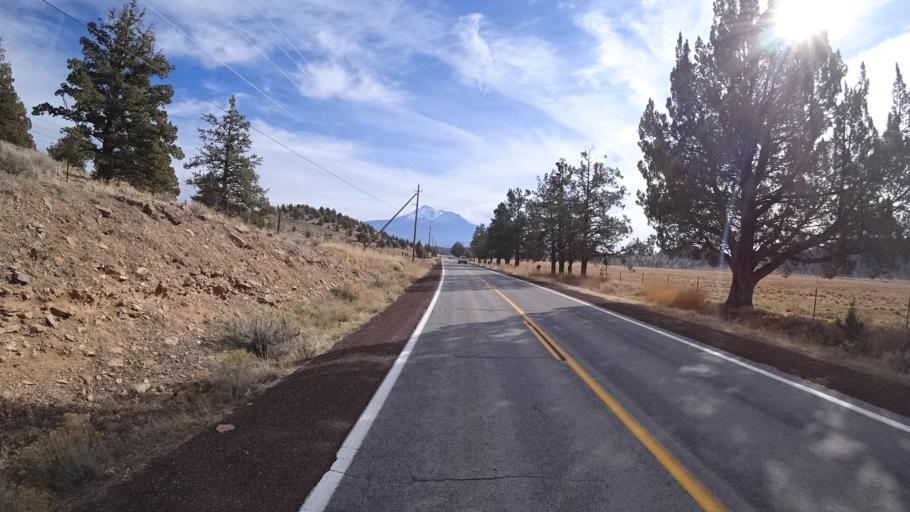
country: US
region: California
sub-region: Siskiyou County
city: Weed
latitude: 41.5747
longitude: -122.3940
